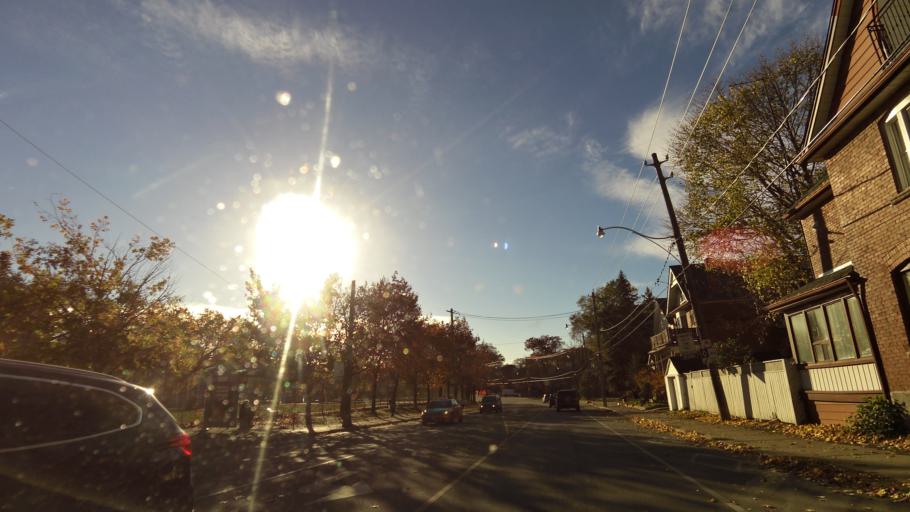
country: CA
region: Ontario
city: Toronto
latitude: 43.6623
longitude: -79.4723
